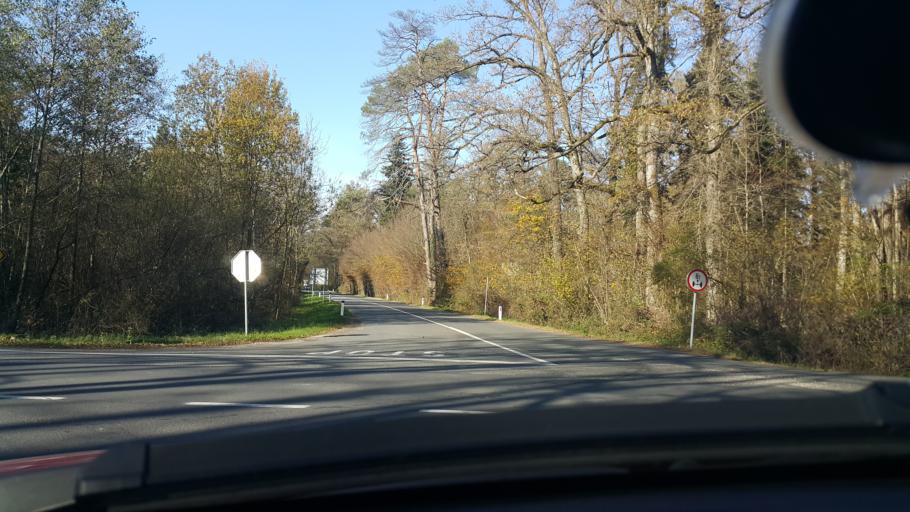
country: SI
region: Brezice
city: Brezice
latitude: 45.9406
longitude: 15.6538
